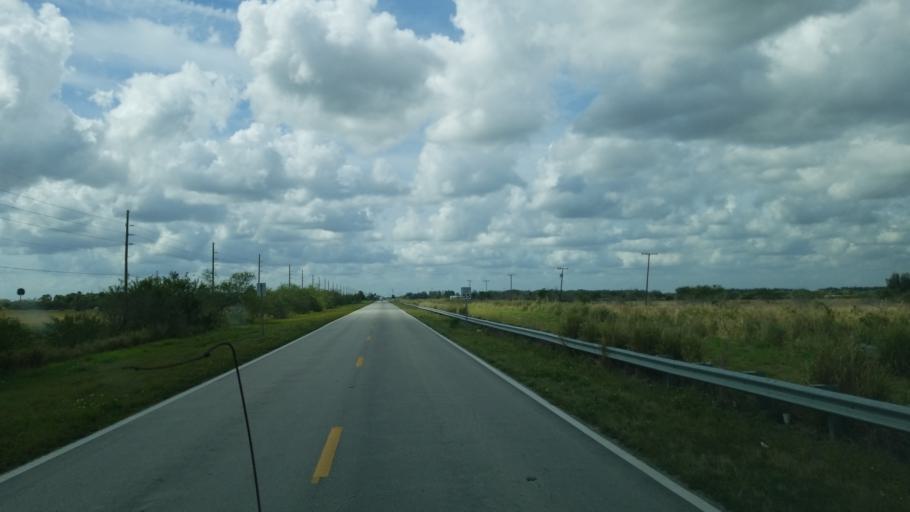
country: US
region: Florida
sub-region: Saint Lucie County
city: Lakewood Park
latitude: 27.4476
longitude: -80.5098
